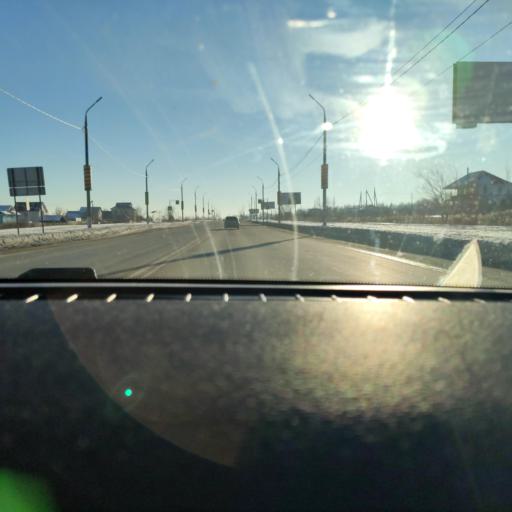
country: RU
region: Samara
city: Novokuybyshevsk
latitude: 53.0797
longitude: 49.9983
